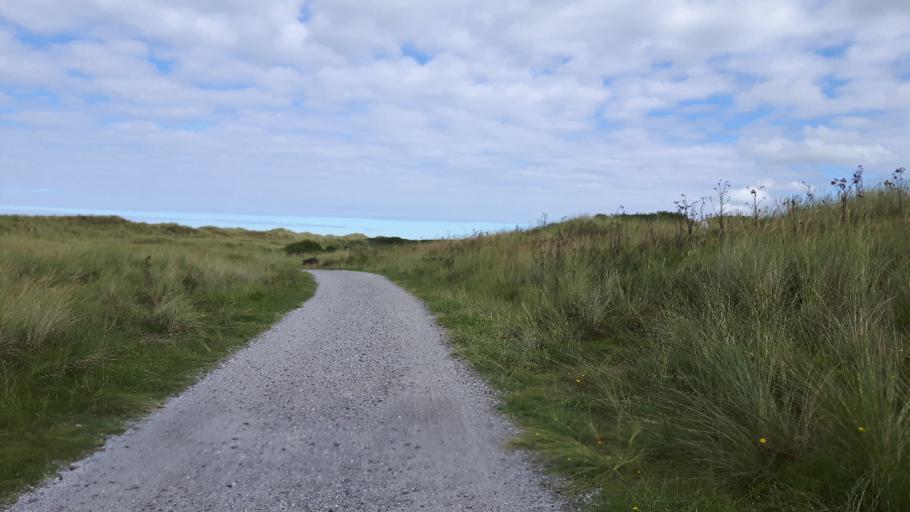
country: NL
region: Friesland
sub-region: Gemeente Ameland
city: Nes
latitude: 53.4571
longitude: 5.7439
